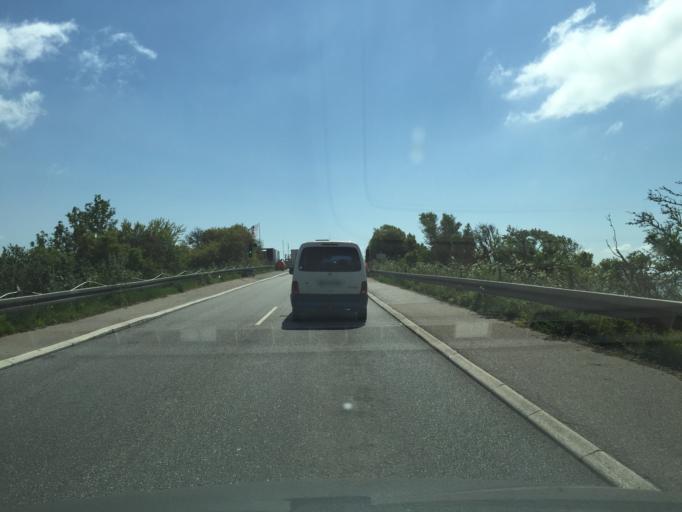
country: DK
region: Zealand
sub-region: Vordingborg Kommune
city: Stege
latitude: 54.9930
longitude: 12.1607
